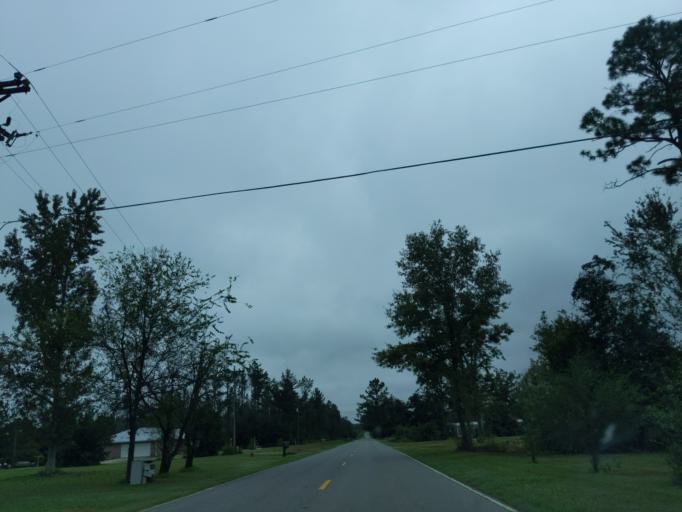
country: US
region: Florida
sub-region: Jackson County
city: Sneads
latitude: 30.7036
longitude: -84.9239
